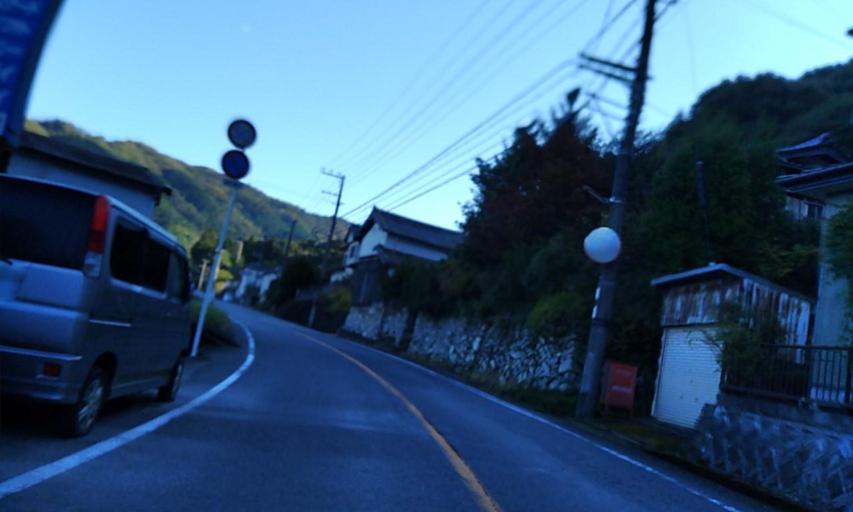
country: JP
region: Wakayama
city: Iwade
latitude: 34.1526
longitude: 135.3182
